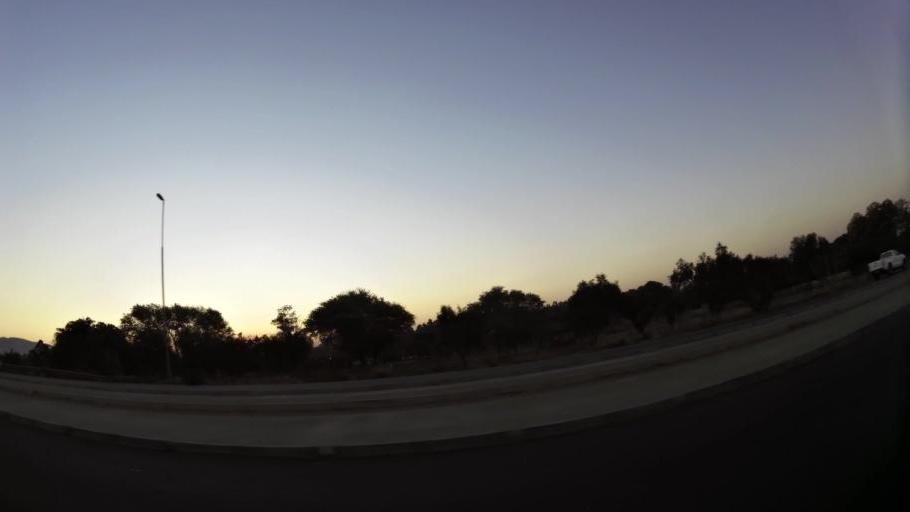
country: ZA
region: North-West
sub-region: Bojanala Platinum District Municipality
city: Rustenburg
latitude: -25.6452
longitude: 27.2584
